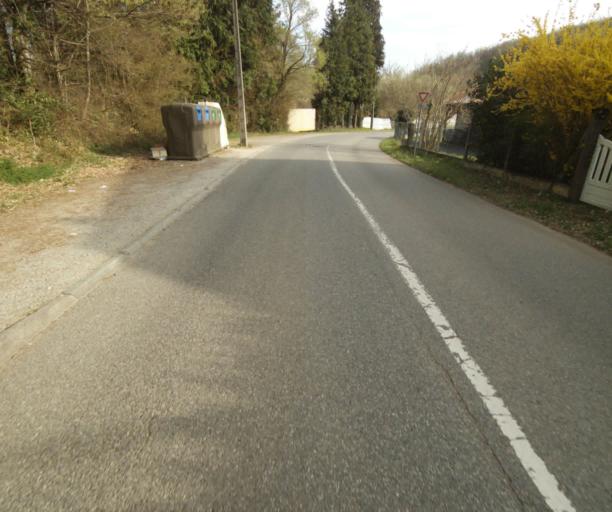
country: FR
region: Limousin
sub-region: Departement de la Correze
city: Tulle
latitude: 45.2875
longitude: 1.7653
